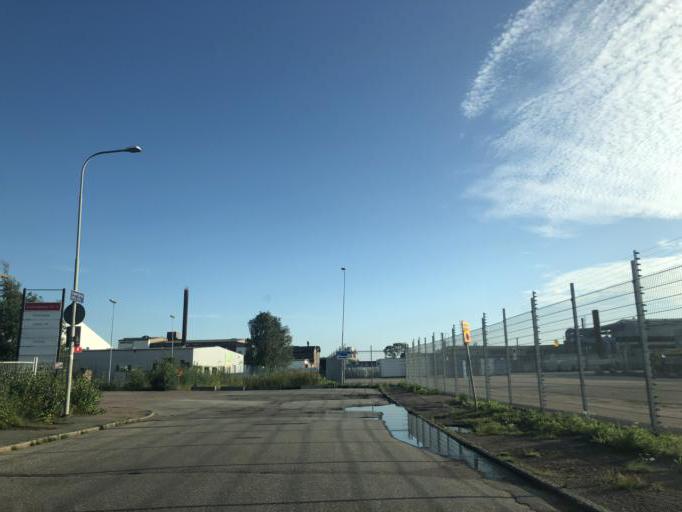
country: SE
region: Vaestra Goetaland
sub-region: Goteborg
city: Goeteborg
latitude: 57.7363
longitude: 11.9925
